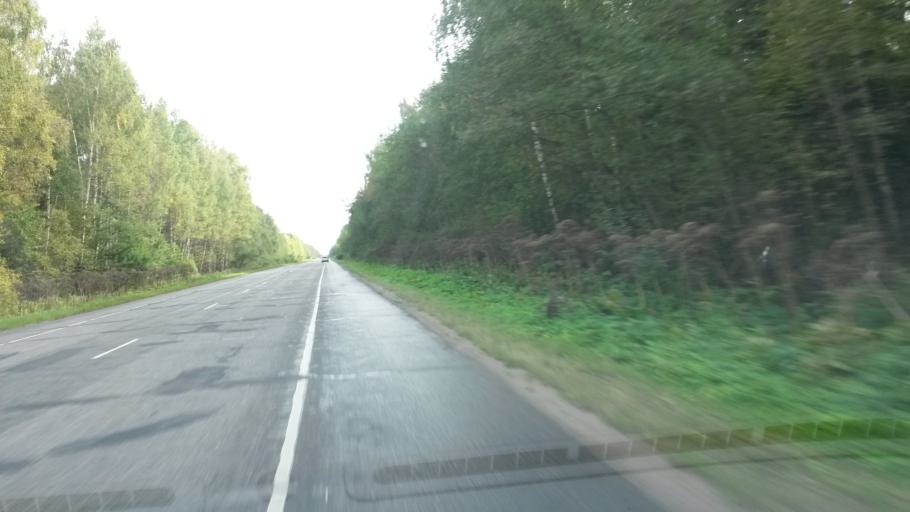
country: RU
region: Ivanovo
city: Kaminskiy
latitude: 57.0779
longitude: 41.4878
